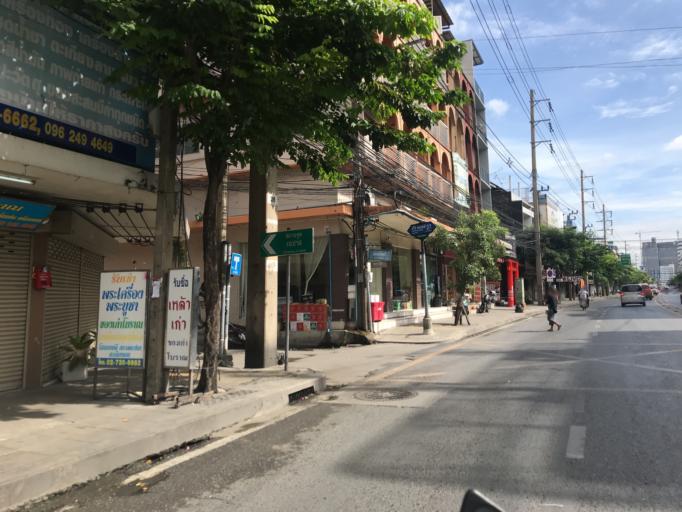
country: TH
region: Bangkok
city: Watthana
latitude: 13.7281
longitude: 100.5959
